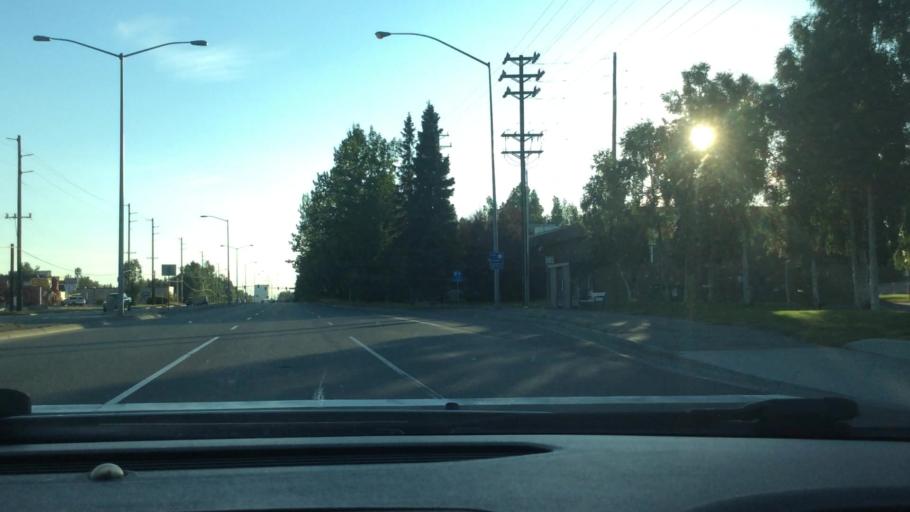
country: US
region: Alaska
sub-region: Anchorage Municipality
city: Anchorage
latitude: 61.1955
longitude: -149.8386
